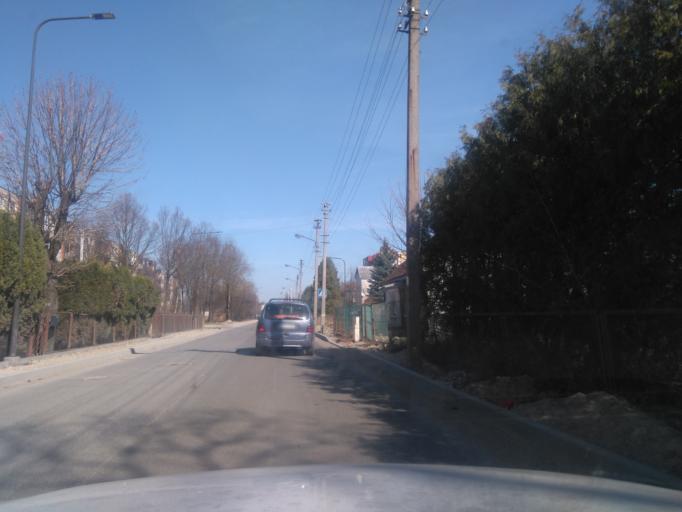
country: LT
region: Kauno apskritis
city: Dainava (Kaunas)
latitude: 54.8902
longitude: 23.9545
